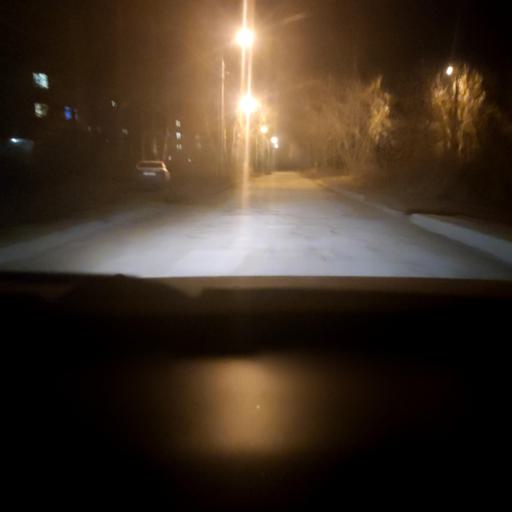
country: RU
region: Perm
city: Polazna
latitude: 58.1369
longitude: 56.3876
